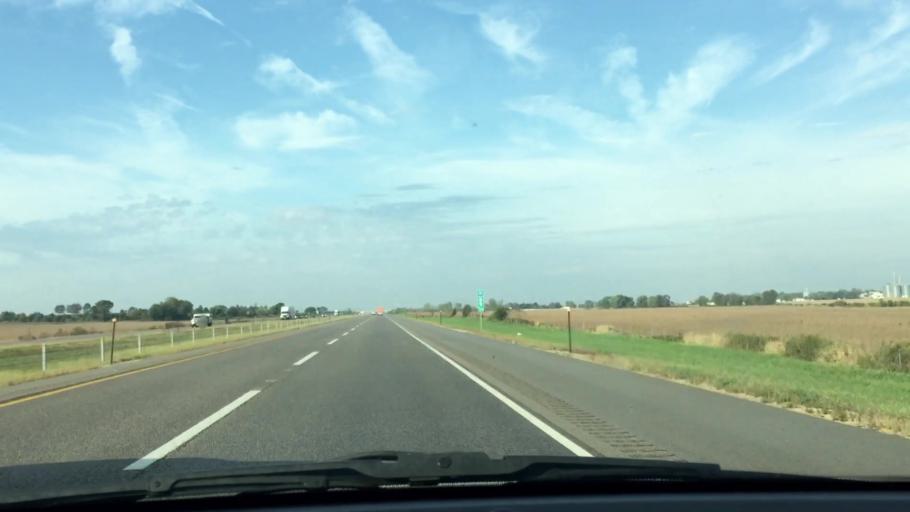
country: US
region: Illinois
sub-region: Lee County
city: Franklin Grove
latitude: 41.8632
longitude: -89.1907
